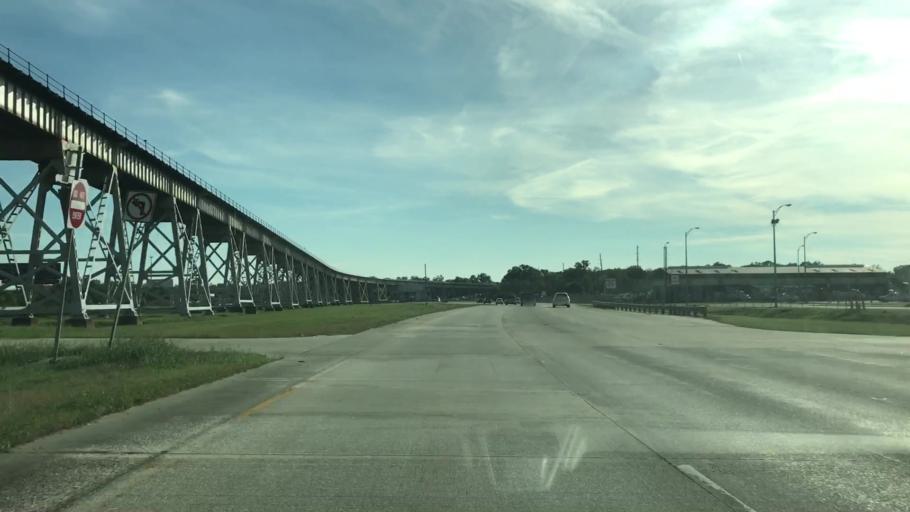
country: US
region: Louisiana
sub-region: Jefferson Parish
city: Bridge City
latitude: 29.9230
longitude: -90.1686
